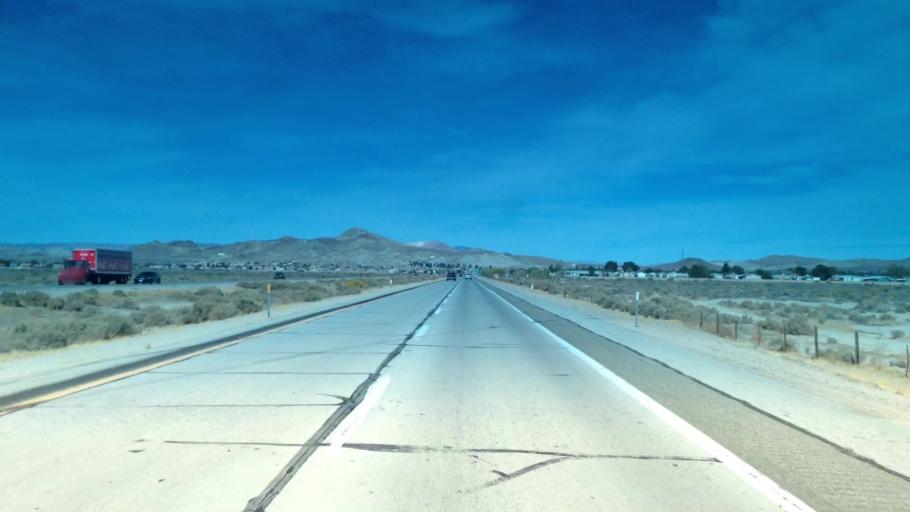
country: US
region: California
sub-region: Kern County
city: Rosamond
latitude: 34.8381
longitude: -118.1710
